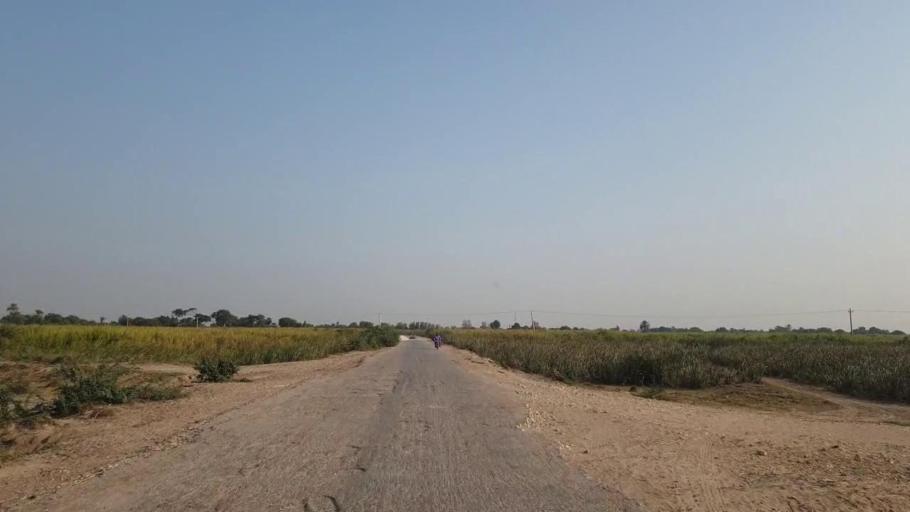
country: PK
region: Sindh
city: Bulri
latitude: 24.9711
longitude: 68.4051
